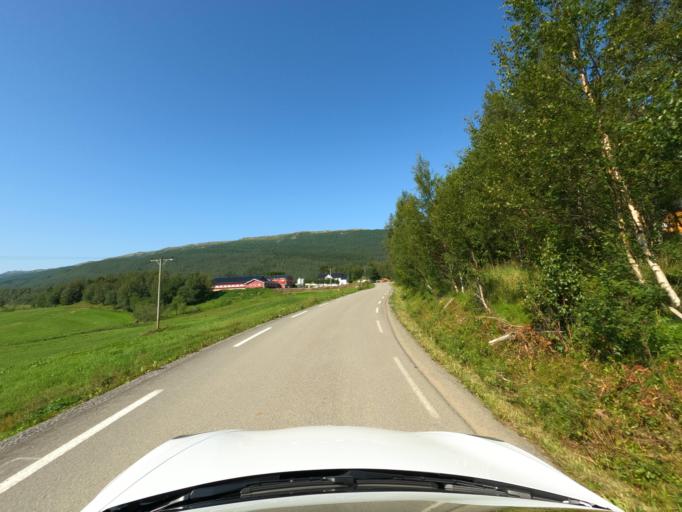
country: NO
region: Nordland
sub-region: Ballangen
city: Ballangen
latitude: 68.3455
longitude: 16.8072
